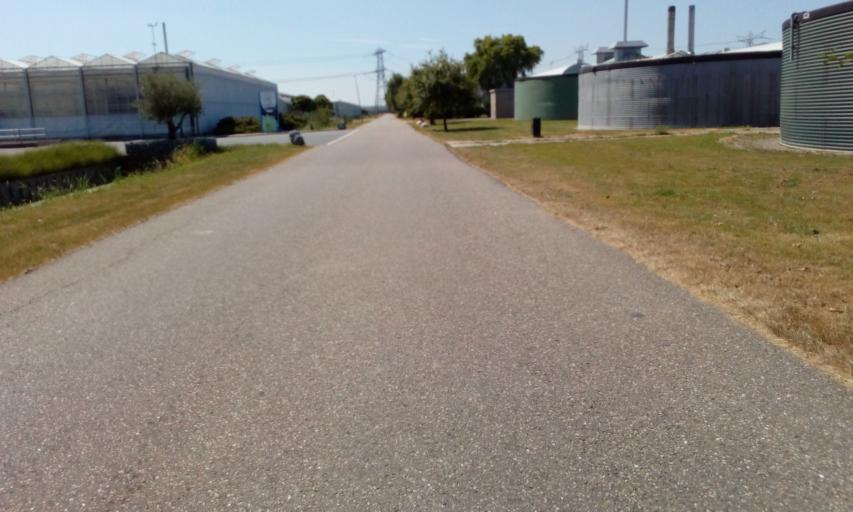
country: NL
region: South Holland
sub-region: Gemeente Westland
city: Naaldwijk
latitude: 51.9876
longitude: 4.2244
